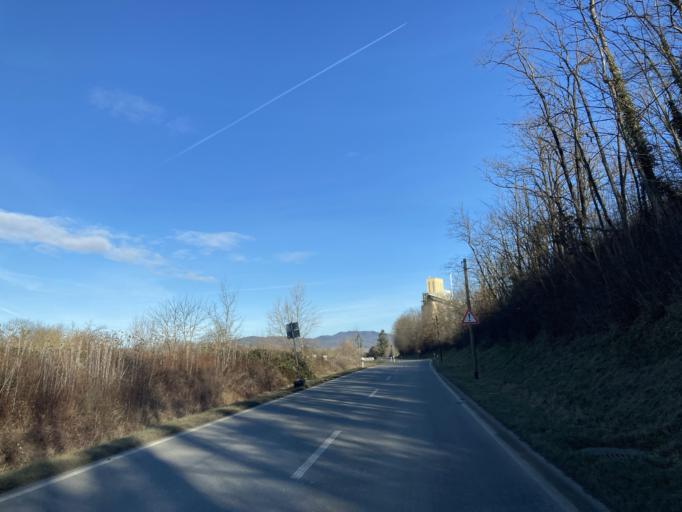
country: DE
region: Baden-Wuerttemberg
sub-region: Freiburg Region
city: Merdingen
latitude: 48.0075
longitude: 7.6702
